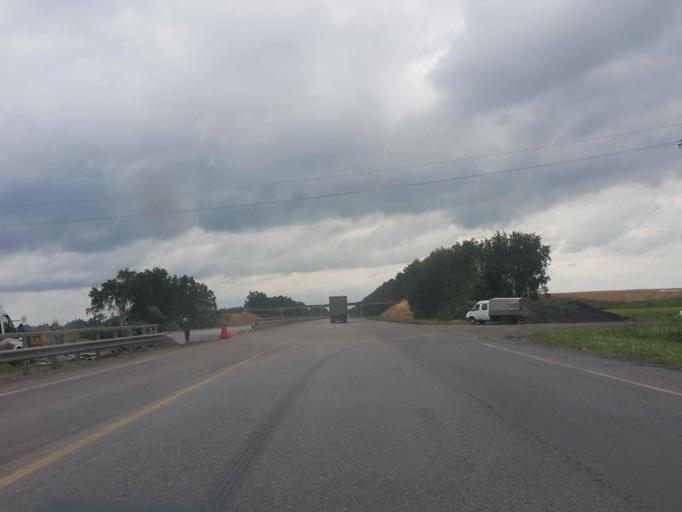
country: RU
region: Tambov
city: Selezni
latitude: 52.8039
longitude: 40.9744
